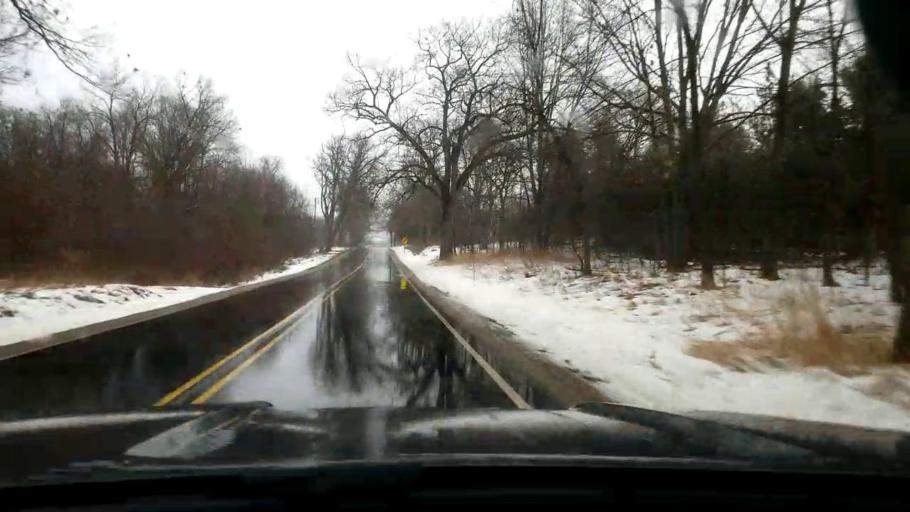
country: US
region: Michigan
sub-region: Jackson County
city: Michigan Center
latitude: 42.3180
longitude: -84.3059
